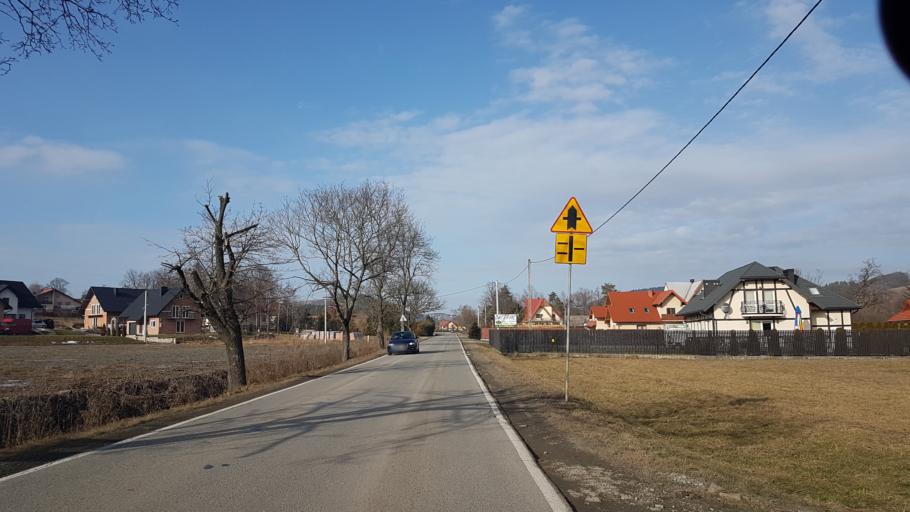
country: PL
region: Lesser Poland Voivodeship
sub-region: Powiat limanowski
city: Lukowica
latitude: 49.6532
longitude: 20.4964
